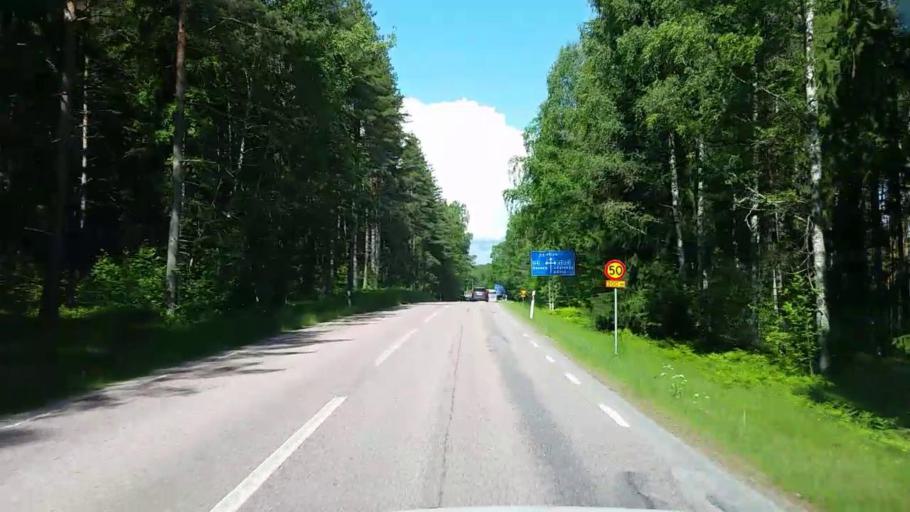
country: SE
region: Vaestmanland
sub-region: Fagersta Kommun
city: Fagersta
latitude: 59.9626
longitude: 15.7704
